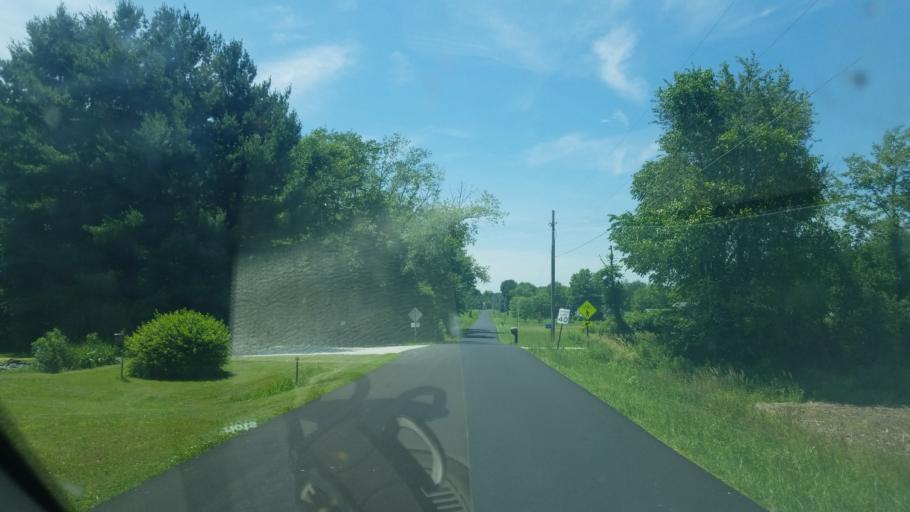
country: US
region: Ohio
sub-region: Stark County
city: Alliance
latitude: 40.8578
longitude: -81.1482
